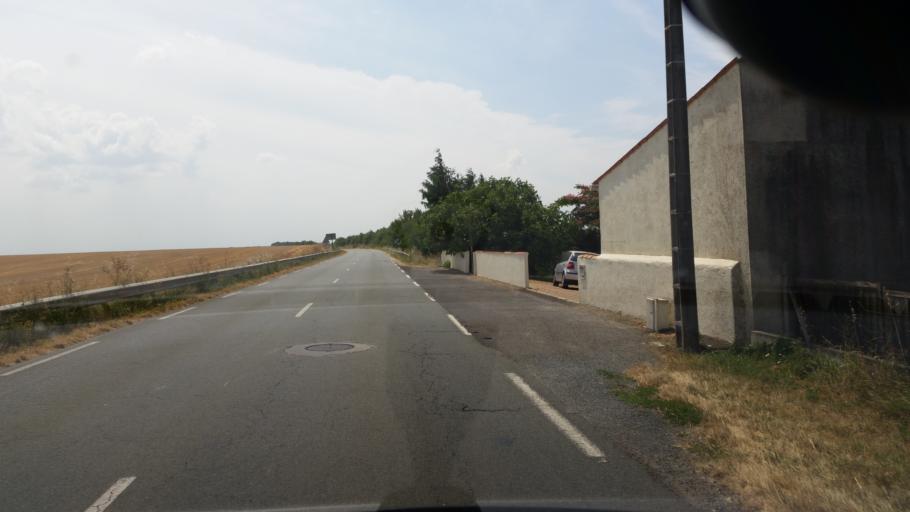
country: FR
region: Poitou-Charentes
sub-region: Departement de la Charente-Maritime
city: Saint-Jean-de-Liversay
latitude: 46.2110
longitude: -0.8755
